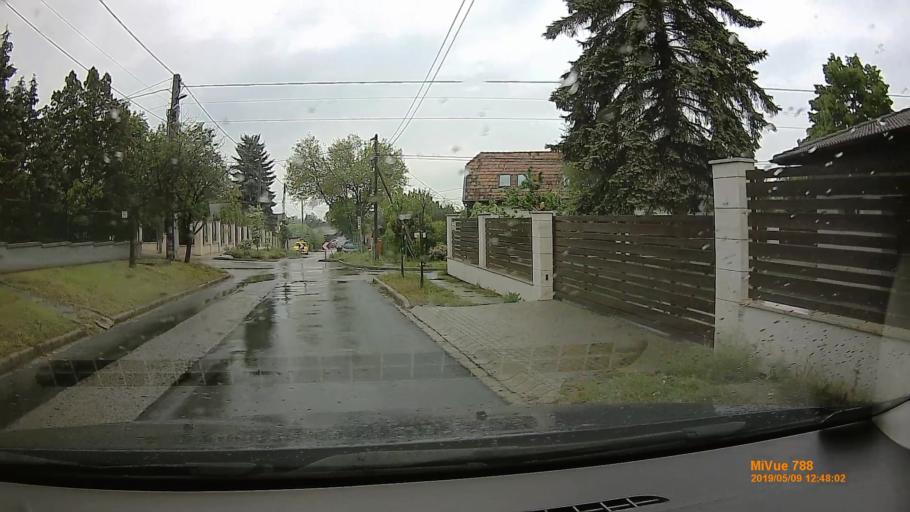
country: HU
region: Budapest
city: Budapest XVI. keruelet
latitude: 47.5375
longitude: 19.1822
